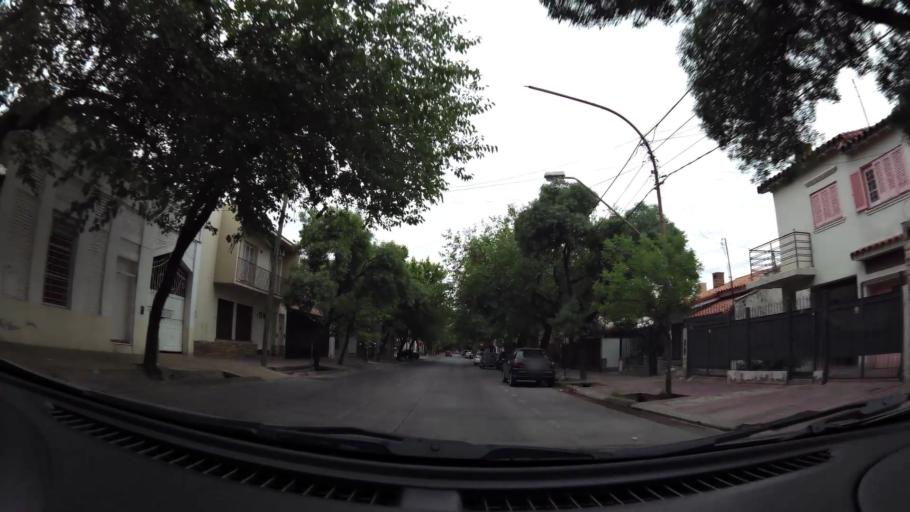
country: AR
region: Mendoza
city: Mendoza
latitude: -32.8847
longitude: -68.8607
